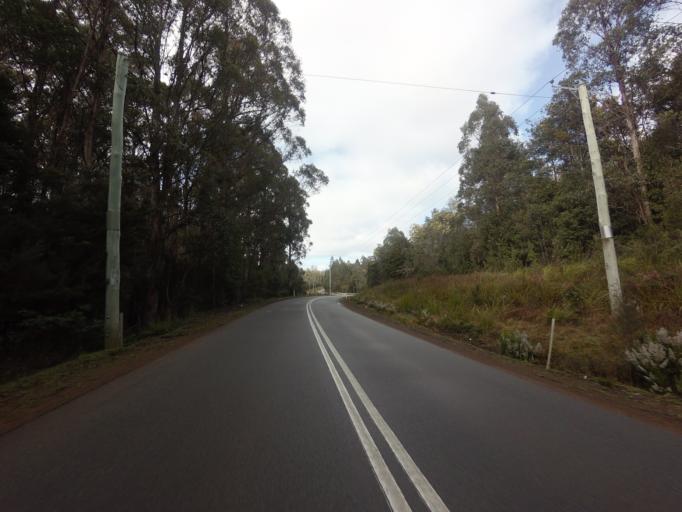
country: AU
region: Tasmania
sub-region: Huon Valley
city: Geeveston
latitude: -43.3642
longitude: 146.9592
